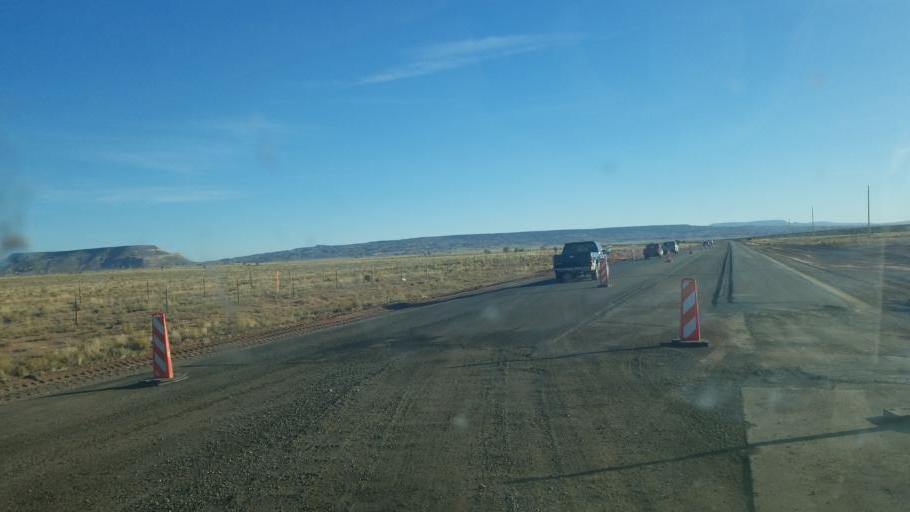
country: US
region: New Mexico
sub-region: Cibola County
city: Laguna
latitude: 34.9651
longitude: -107.1754
